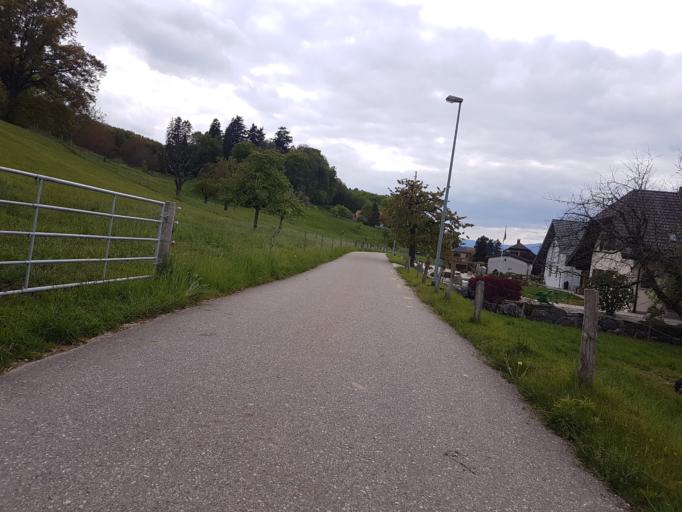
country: CH
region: Bern
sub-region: Seeland District
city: Leuzigen
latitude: 47.1741
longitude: 7.4522
